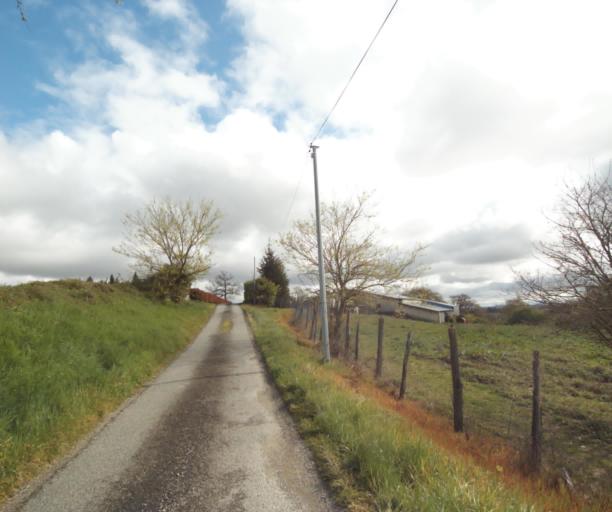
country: FR
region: Midi-Pyrenees
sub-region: Departement de l'Ariege
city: Saverdun
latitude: 43.2133
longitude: 1.5645
